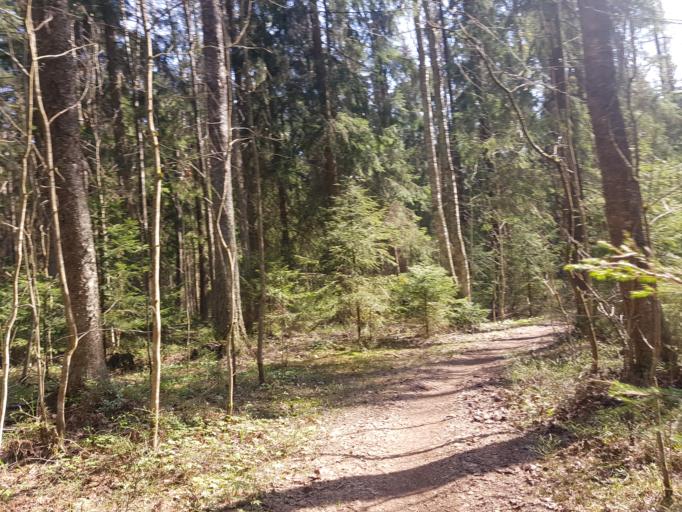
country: FI
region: Uusimaa
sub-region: Helsinki
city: Helsinki
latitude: 60.2665
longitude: 24.9188
